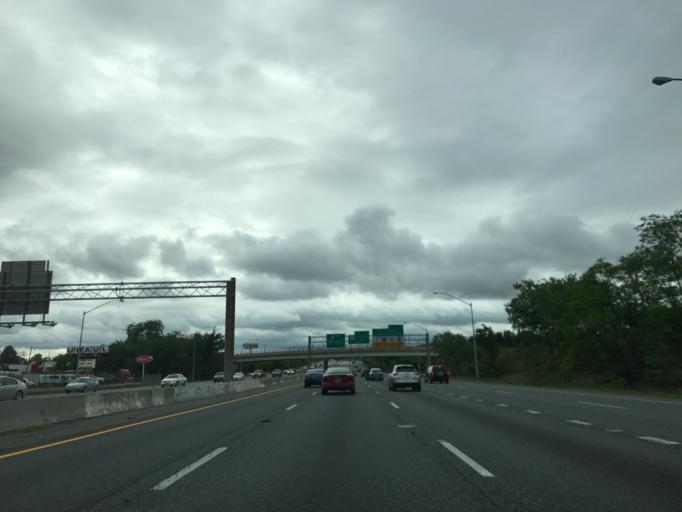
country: US
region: Maryland
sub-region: Prince George's County
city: Glenarden
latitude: 38.9448
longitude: -76.8679
